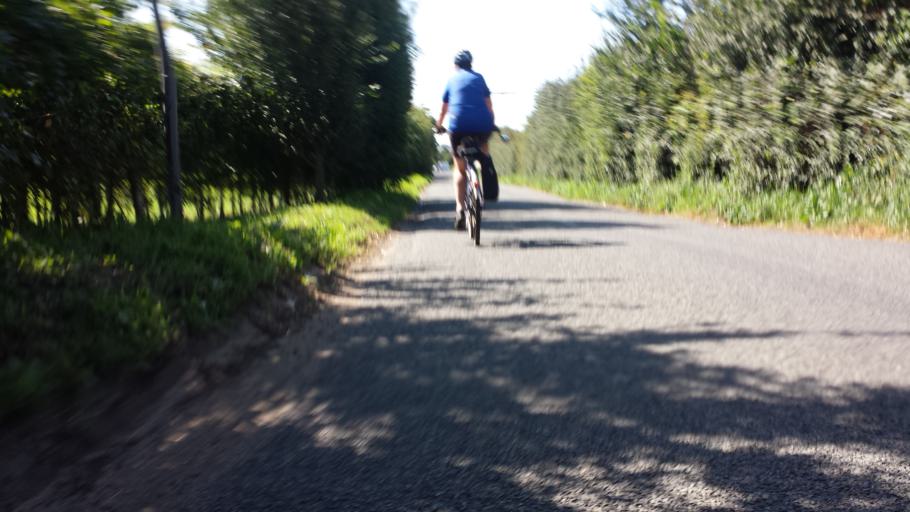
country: GB
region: England
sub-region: Cambridgeshire
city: Isleham
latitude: 52.3434
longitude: 0.4587
